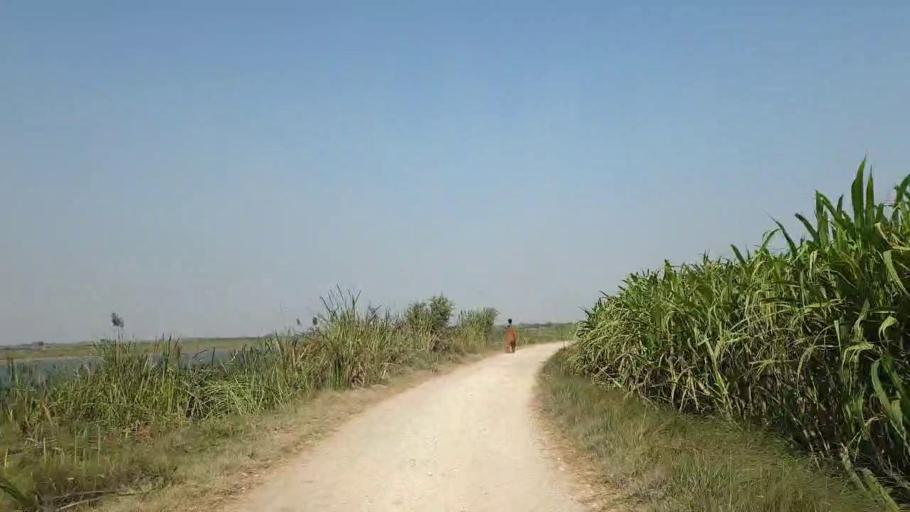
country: PK
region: Sindh
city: Bulri
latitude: 24.9332
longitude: 68.3822
